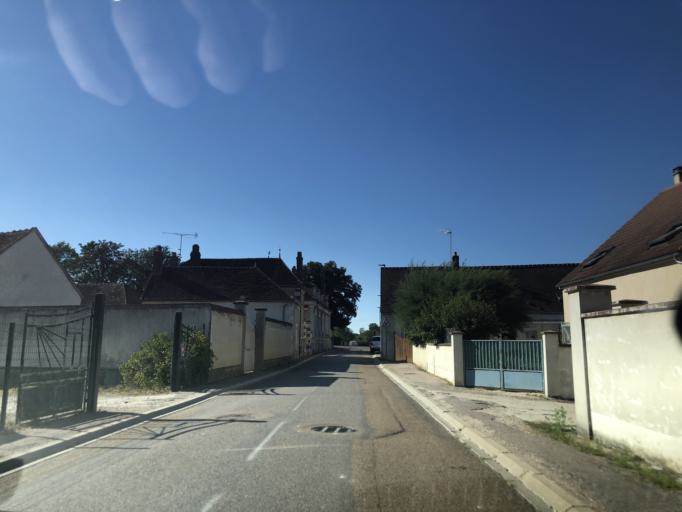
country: FR
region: Bourgogne
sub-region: Departement de l'Yonne
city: Cheny
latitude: 47.9269
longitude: 3.5210
